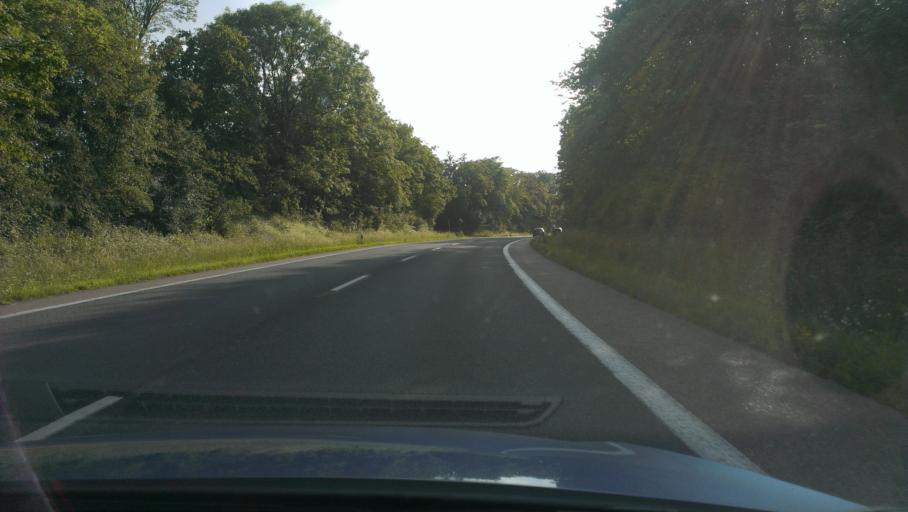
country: DE
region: North Rhine-Westphalia
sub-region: Regierungsbezirk Munster
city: Ennigerloh
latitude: 51.7927
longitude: 7.9801
